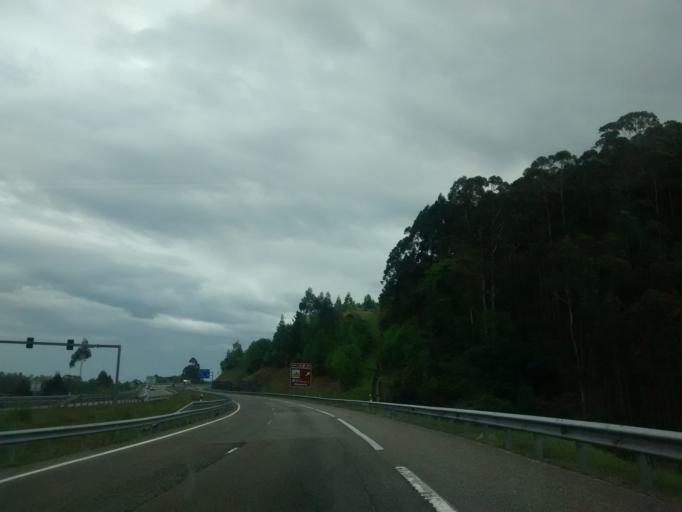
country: ES
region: Asturias
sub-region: Province of Asturias
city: Ribadesella
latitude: 43.4619
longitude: -5.1396
